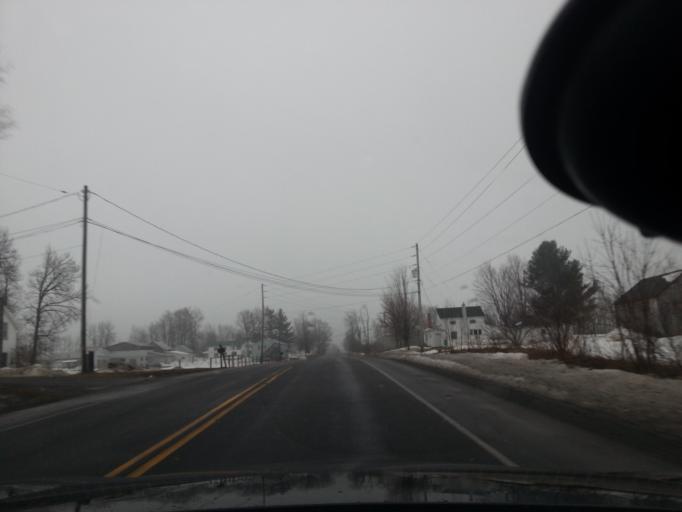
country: US
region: New York
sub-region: St. Lawrence County
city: Ogdensburg
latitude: 44.6099
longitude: -75.3972
